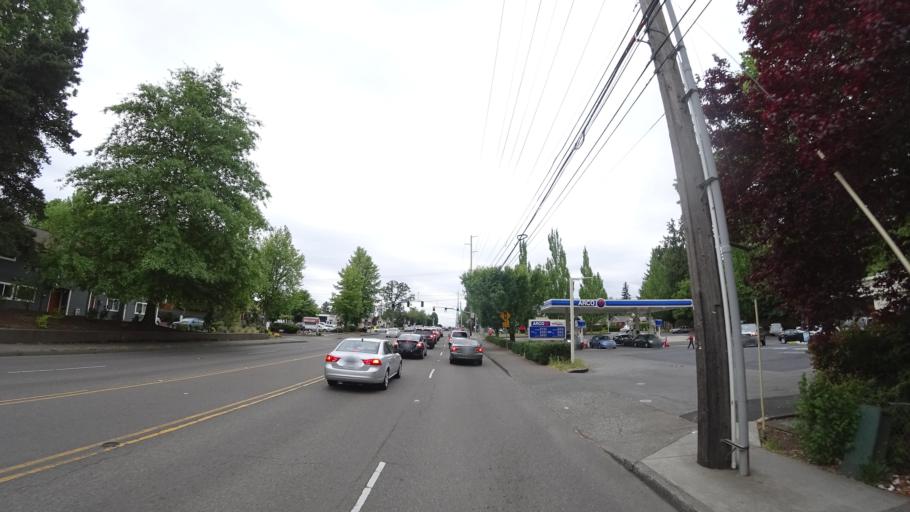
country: US
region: Oregon
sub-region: Washington County
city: Beaverton
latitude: 45.4766
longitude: -122.7991
